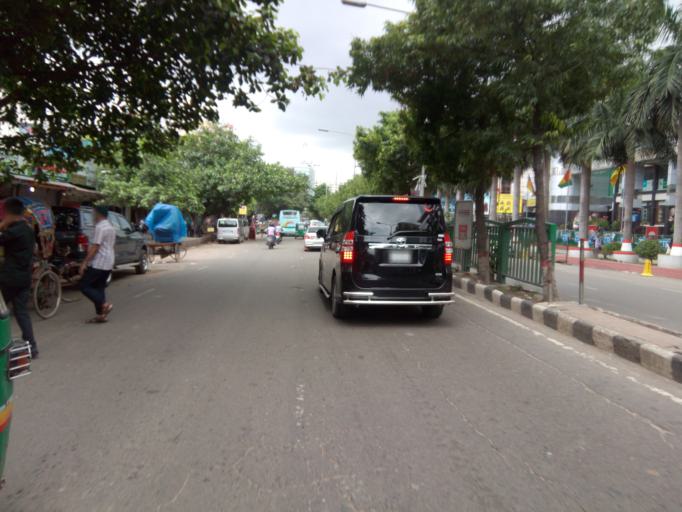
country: BD
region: Dhaka
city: Azimpur
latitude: 23.7504
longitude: 90.3906
